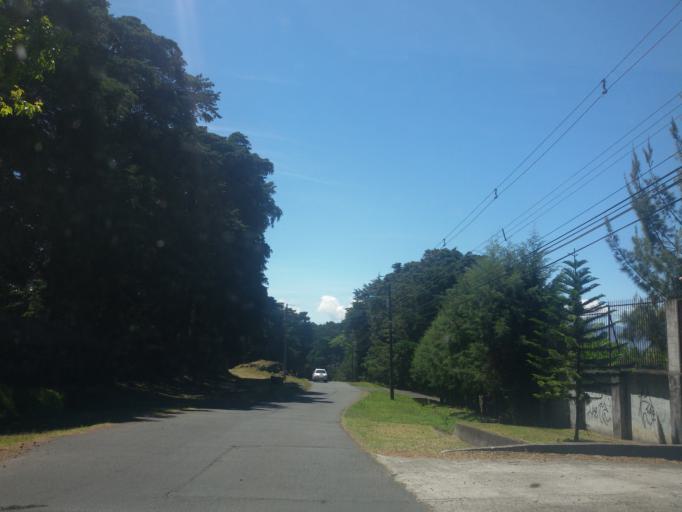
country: CR
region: Heredia
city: San Josecito
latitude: 10.0541
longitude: -84.0888
